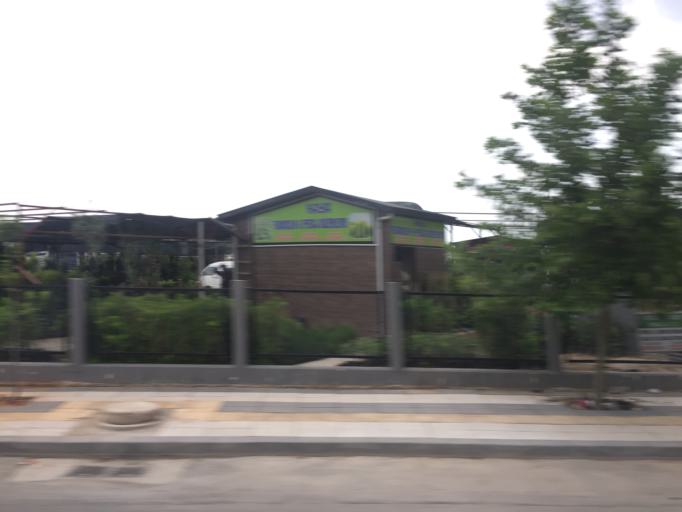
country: TR
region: Gaziantep
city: Gaziantep
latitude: 37.0603
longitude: 37.4156
